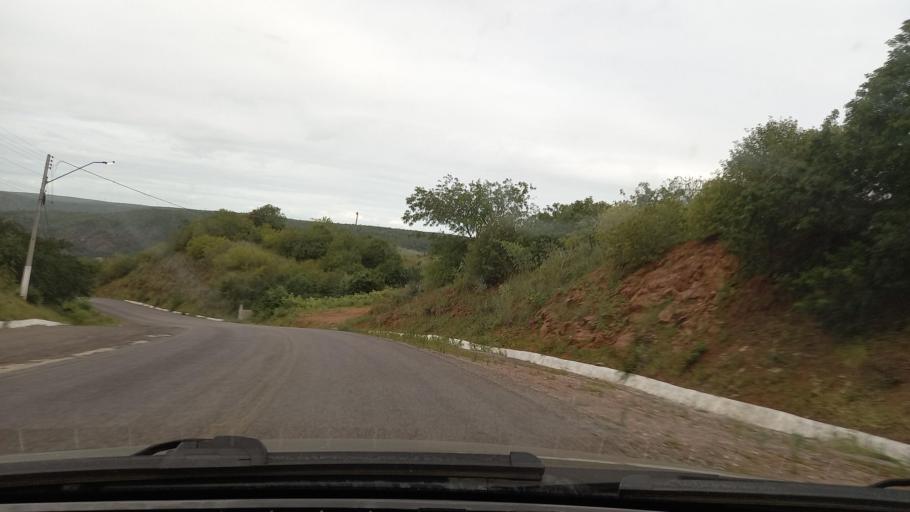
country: BR
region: Sergipe
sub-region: Caninde De Sao Francisco
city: Caninde de Sao Francisco
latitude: -9.6196
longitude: -37.7615
